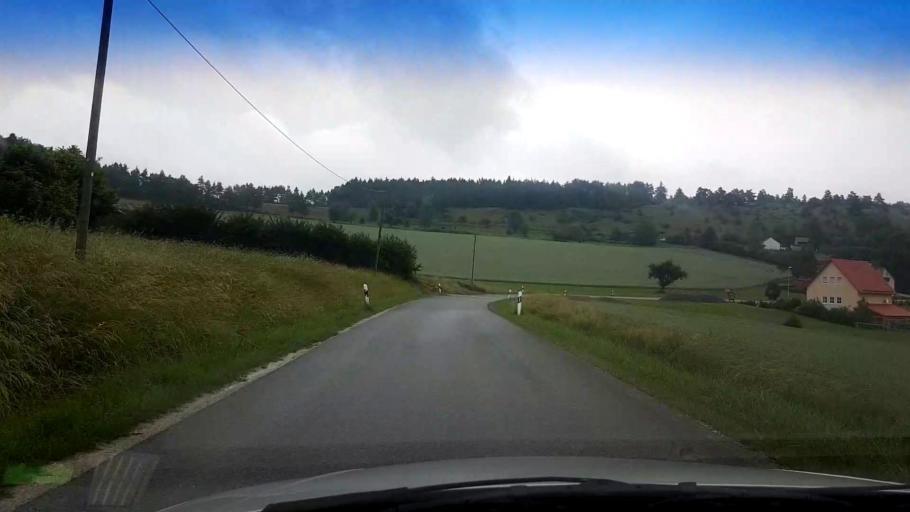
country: DE
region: Bavaria
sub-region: Upper Franconia
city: Altendorf
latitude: 50.0728
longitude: 11.1605
